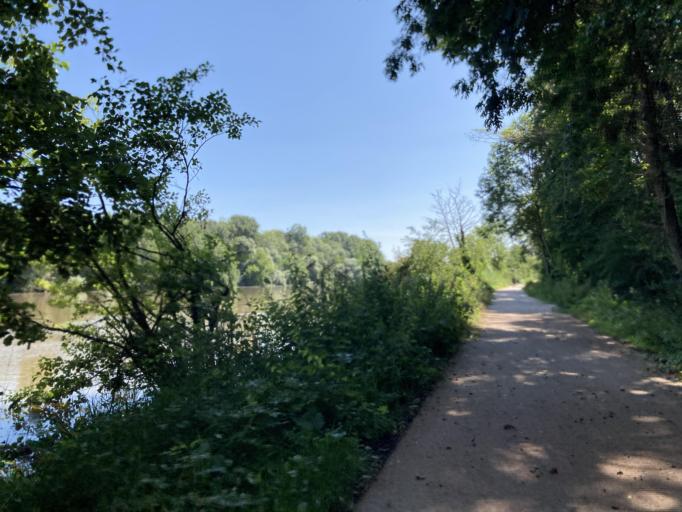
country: FR
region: Bourgogne
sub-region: Departement de l'Yonne
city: Joigny
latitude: 47.9684
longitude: 3.4334
